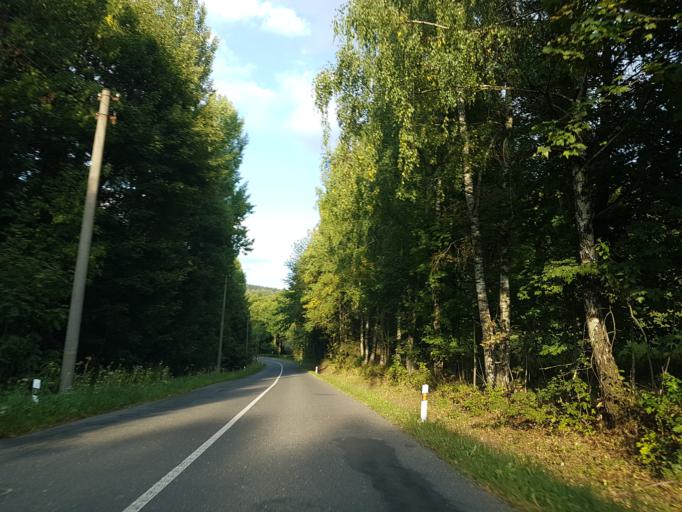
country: CZ
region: Liberecky
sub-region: Okres Jablonec nad Nisou
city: Jablonec nad Nisou
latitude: 50.6932
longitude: 15.1902
